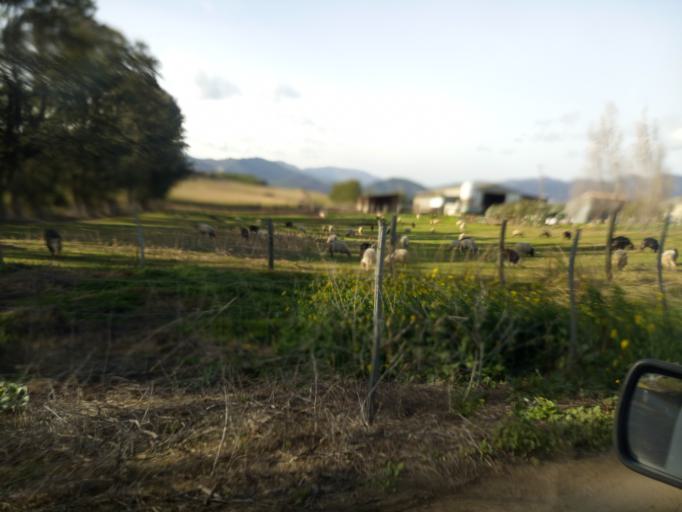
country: FR
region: Corsica
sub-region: Departement de la Haute-Corse
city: Linguizzetta
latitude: 42.2658
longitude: 9.5440
